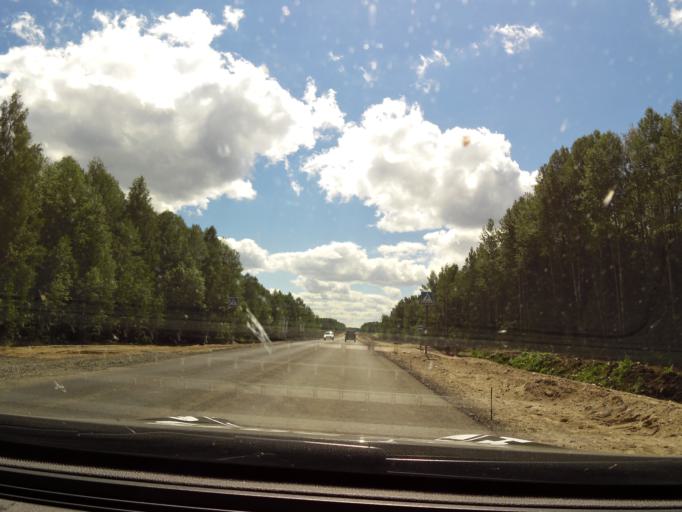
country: RU
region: Vologda
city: Molochnoye
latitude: 59.3616
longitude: 39.6737
